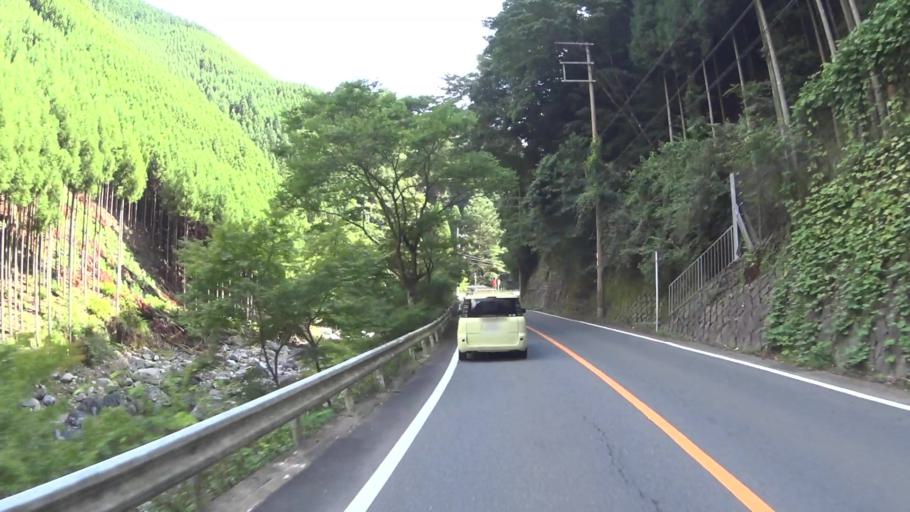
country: JP
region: Kyoto
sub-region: Kyoto-shi
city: Kamigyo-ku
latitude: 35.0628
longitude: 135.6809
